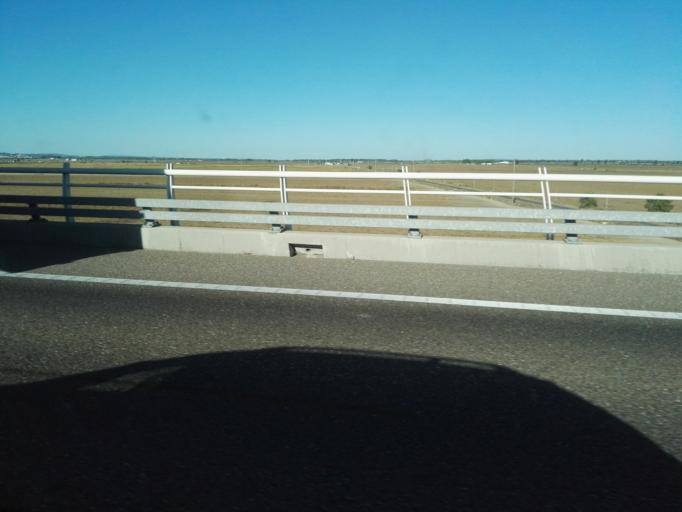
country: PT
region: Santarem
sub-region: Benavente
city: Samora Correia
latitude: 38.9844
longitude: -8.8883
